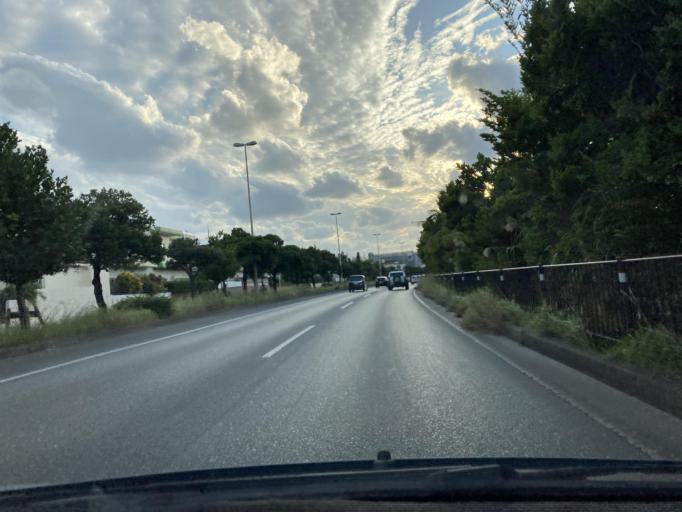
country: JP
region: Okinawa
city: Ginowan
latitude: 26.2808
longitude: 127.7414
